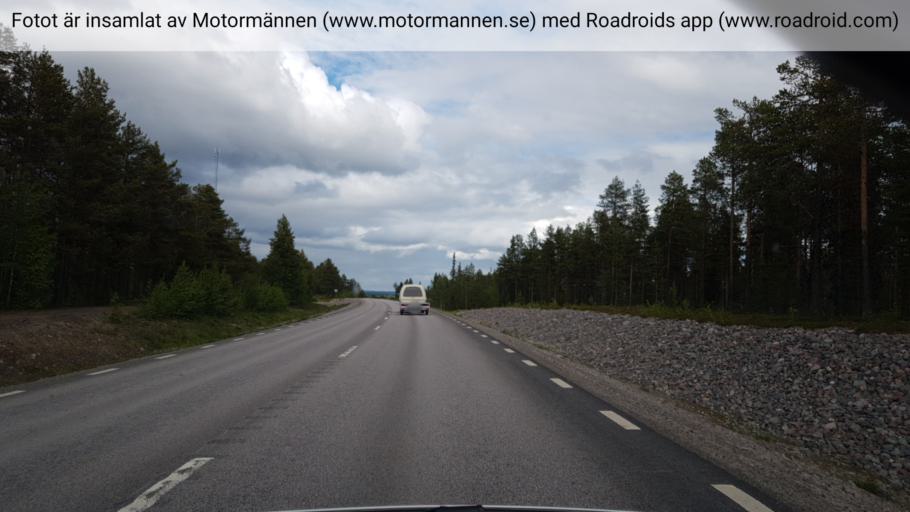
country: SE
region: Norrbotten
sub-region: Gallivare Kommun
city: Malmberget
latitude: 67.6659
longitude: 21.5971
